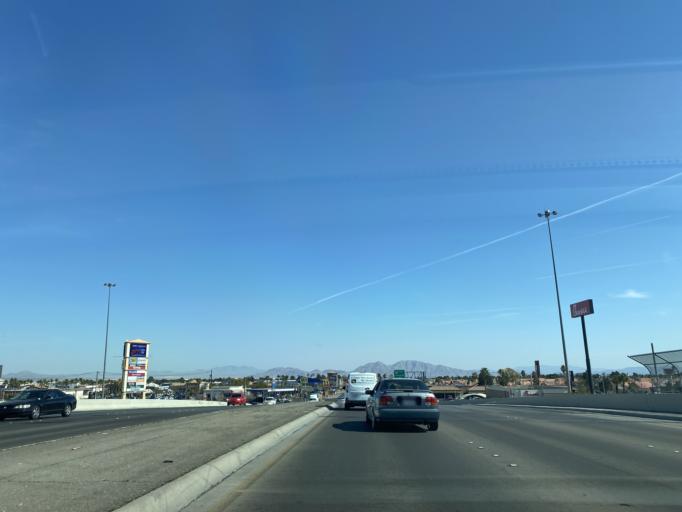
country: US
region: Nevada
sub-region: Clark County
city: Spring Valley
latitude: 36.1969
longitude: -115.2452
